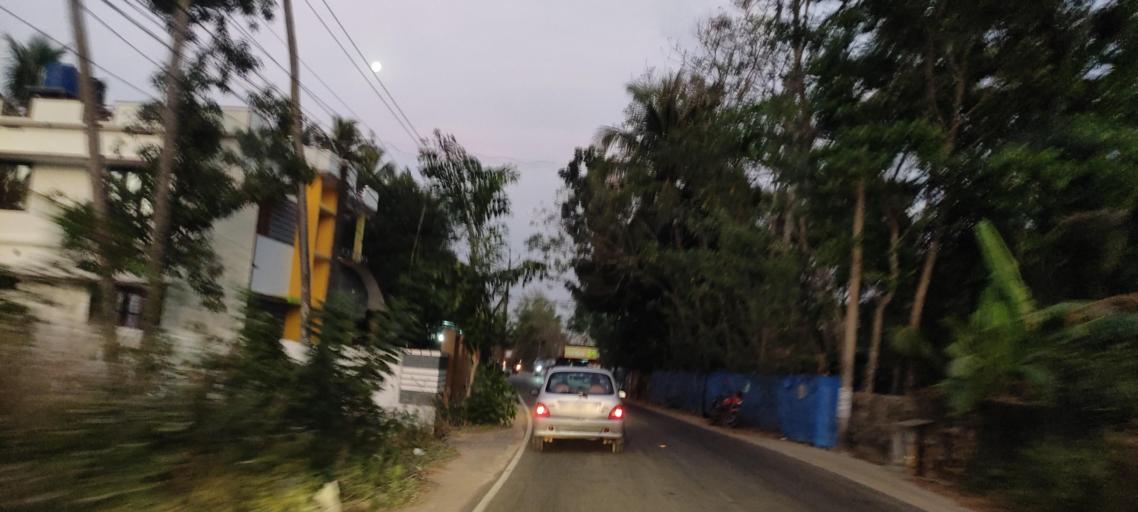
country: IN
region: Kerala
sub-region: Alappuzha
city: Kutiatodu
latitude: 9.7732
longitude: 76.3521
